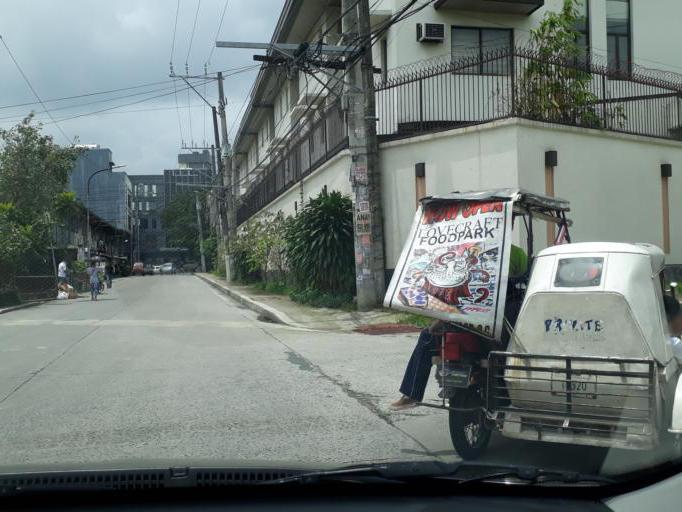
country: PH
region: Metro Manila
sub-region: San Juan
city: San Juan
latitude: 14.6233
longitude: 121.0387
